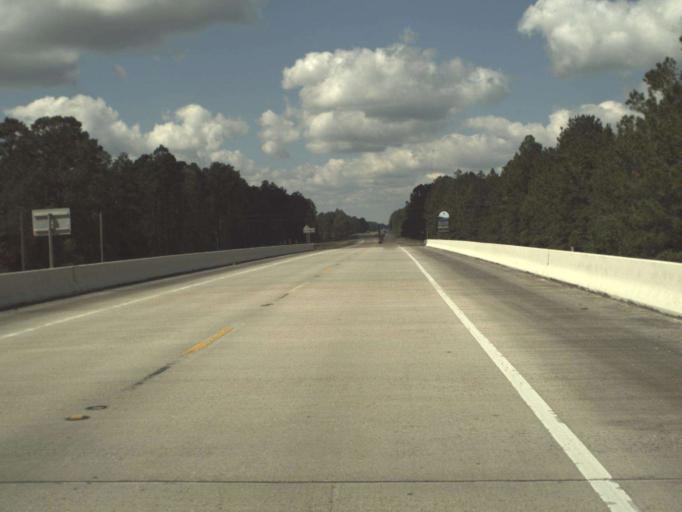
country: US
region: Florida
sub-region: Bay County
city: Laguna Beach
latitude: 30.4514
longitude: -85.8991
